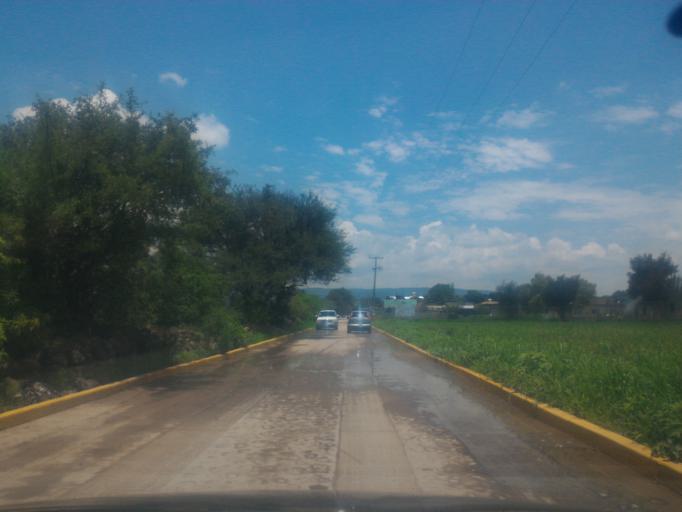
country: MX
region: Guanajuato
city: Ciudad Manuel Doblado
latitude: 20.7987
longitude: -101.9918
